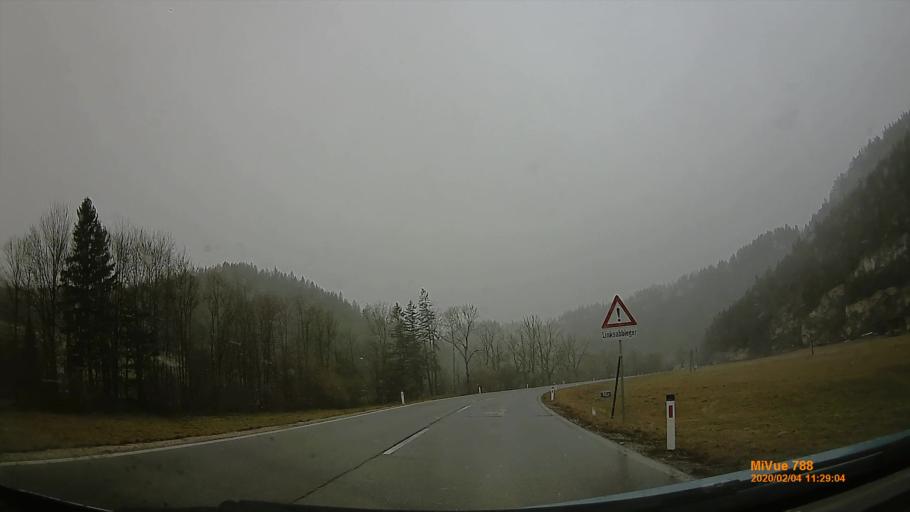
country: AT
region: Styria
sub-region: Politischer Bezirk Bruck-Muerzzuschlag
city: Kapellen
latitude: 47.6510
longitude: 15.6194
